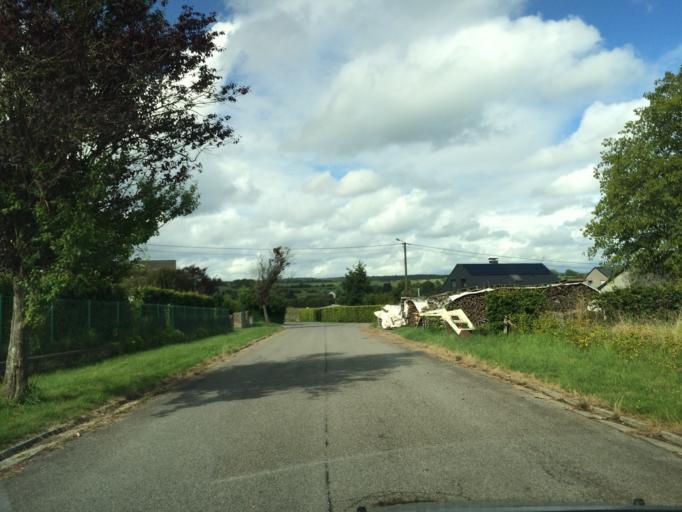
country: BE
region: Wallonia
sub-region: Province du Luxembourg
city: Chiny
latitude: 49.7008
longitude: 5.3718
